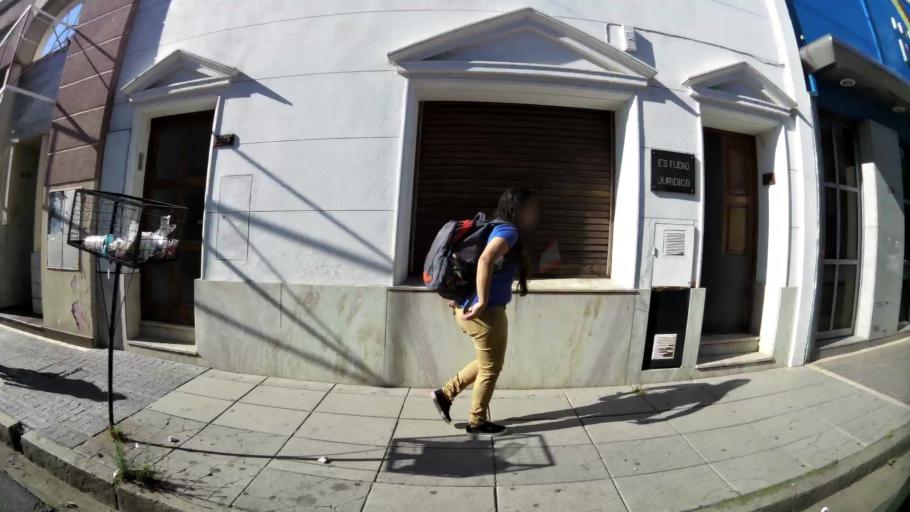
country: AR
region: Santa Fe
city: Santa Fe de la Vera Cruz
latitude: -31.6452
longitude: -60.7083
